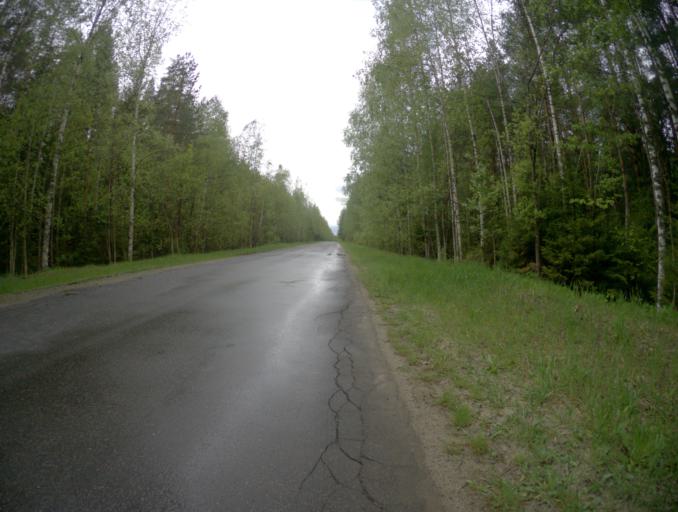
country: RU
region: Vladimir
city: Zolotkovo
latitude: 55.3461
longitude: 40.9772
